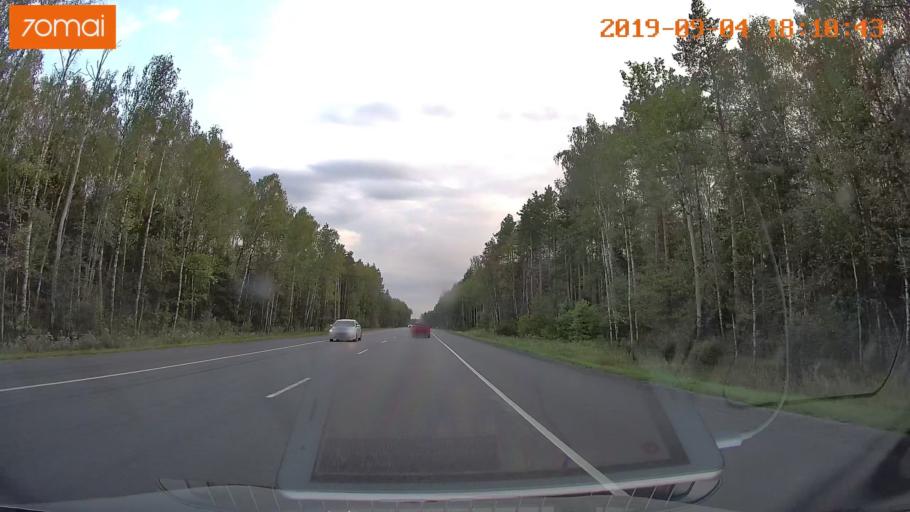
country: RU
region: Moskovskaya
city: Lopatinskiy
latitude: 55.3850
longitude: 38.7622
